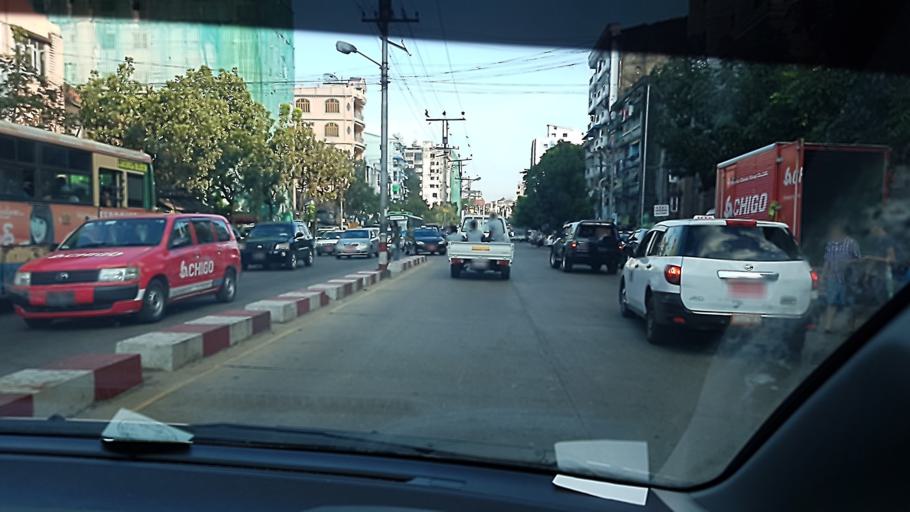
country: MM
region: Yangon
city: Yangon
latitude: 16.8112
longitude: 96.1724
